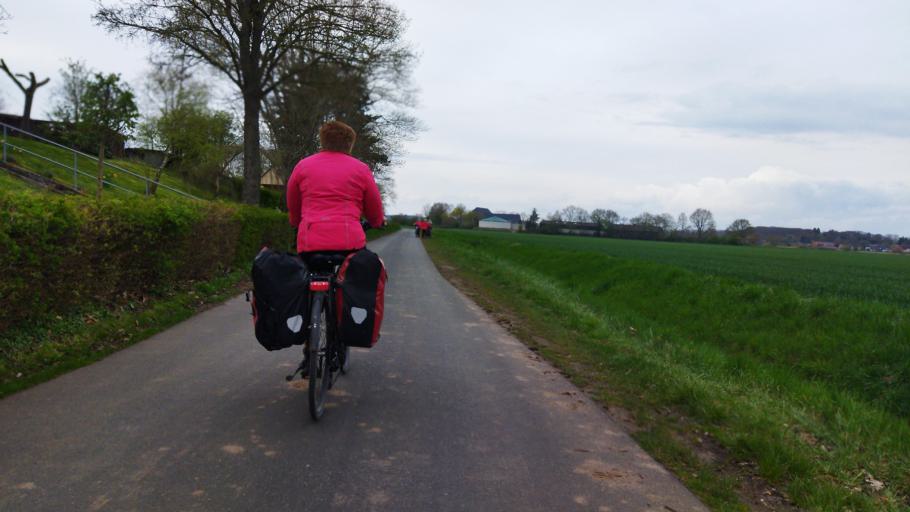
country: DE
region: Lower Saxony
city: Ahsen-Oetzen
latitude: 52.9837
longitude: 9.1217
